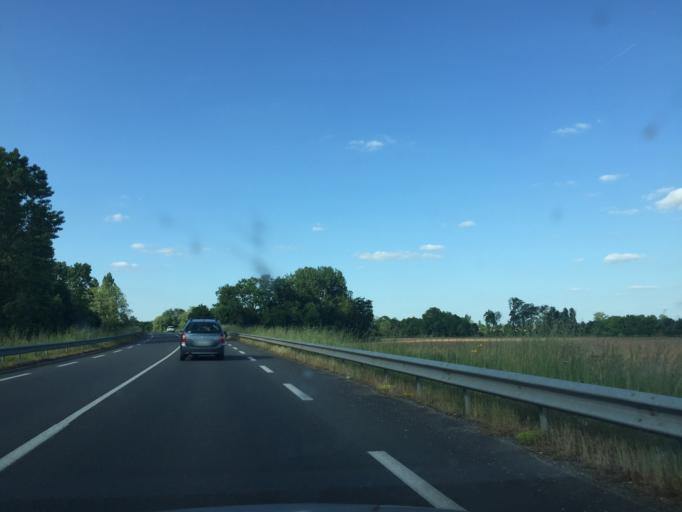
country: FR
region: Aquitaine
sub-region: Departement de la Gironde
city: Coutras
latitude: 45.0308
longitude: -0.1481
